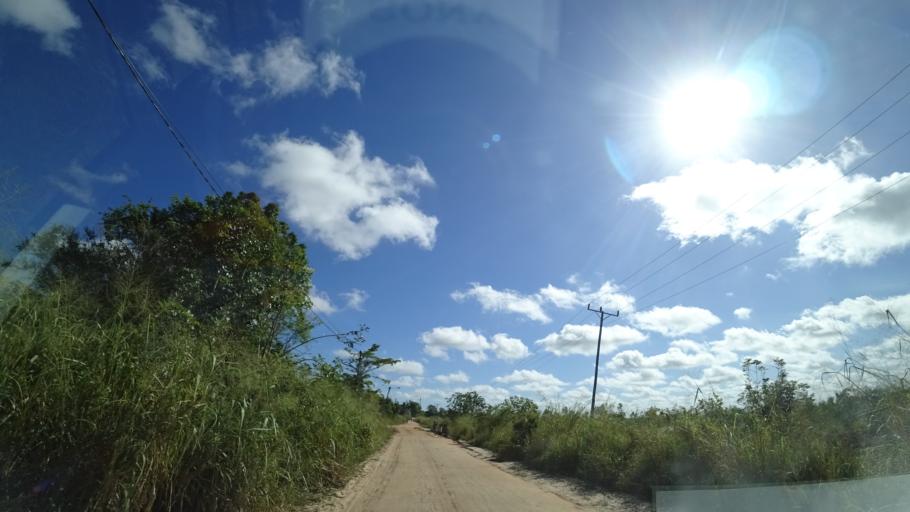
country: MZ
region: Sofala
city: Dondo
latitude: -19.3929
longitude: 34.7086
